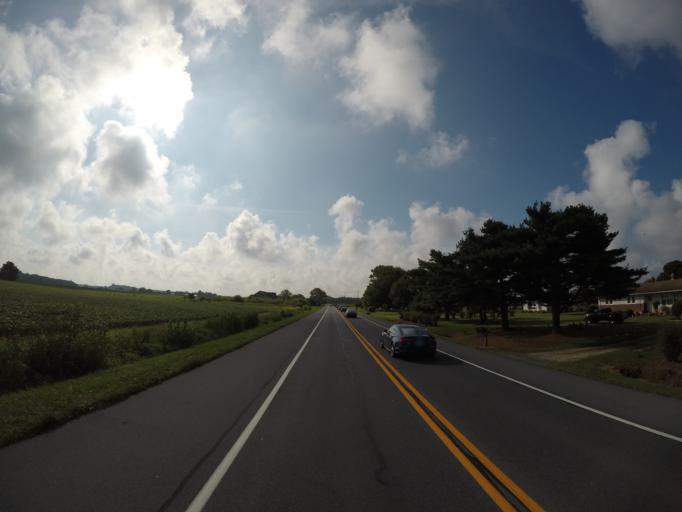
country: US
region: Delaware
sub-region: Sussex County
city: Bridgeville
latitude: 38.7586
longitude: -75.6354
